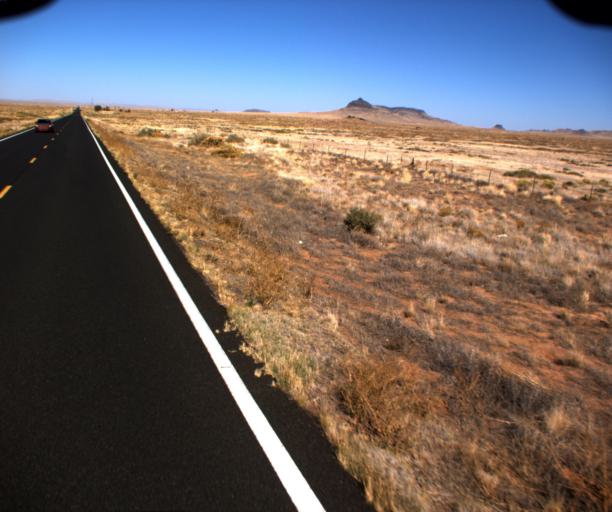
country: US
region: Arizona
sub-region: Navajo County
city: Dilkon
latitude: 35.4841
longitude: -110.4286
